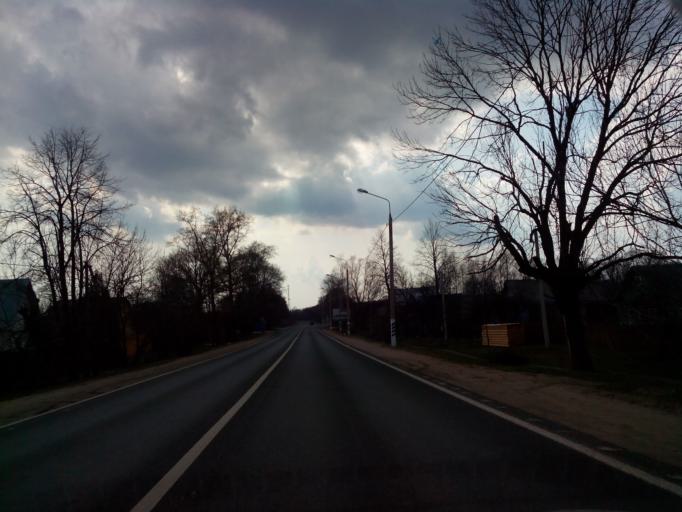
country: RU
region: Moskovskaya
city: Vereya
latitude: 55.5050
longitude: 36.2077
